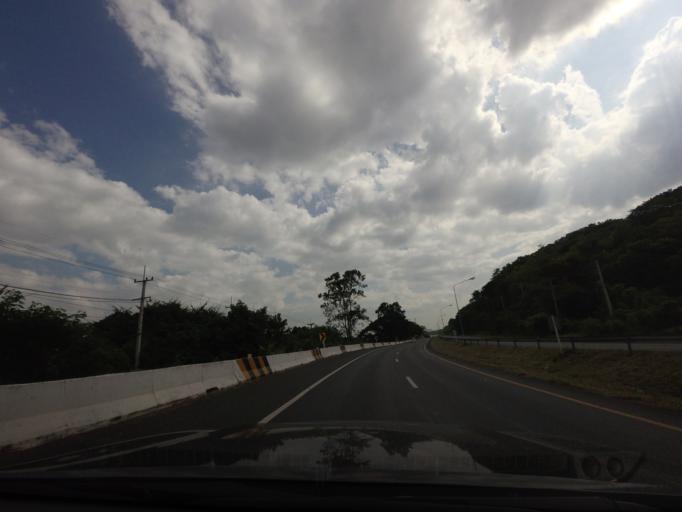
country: TH
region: Lop Buri
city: Chai Badan
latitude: 15.2971
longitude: 101.1296
